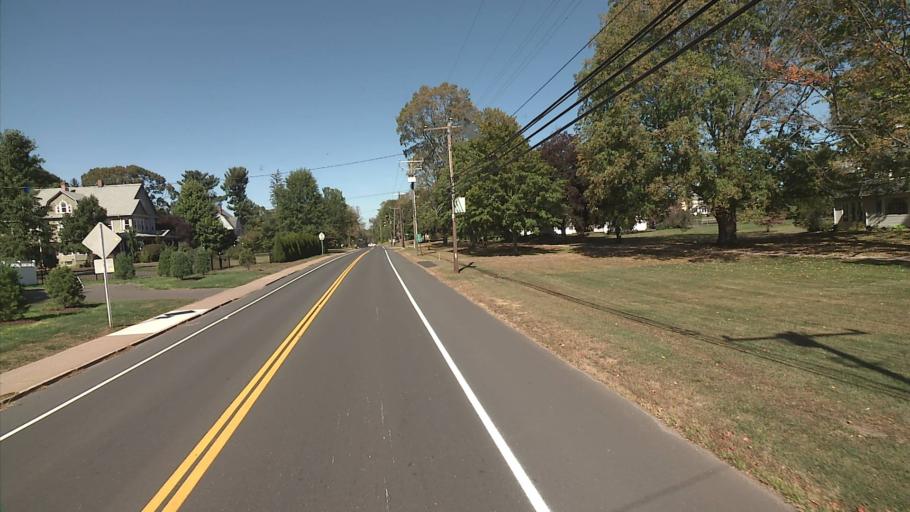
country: US
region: Connecticut
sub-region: Hartford County
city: Manchester
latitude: 41.7560
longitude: -72.5205
